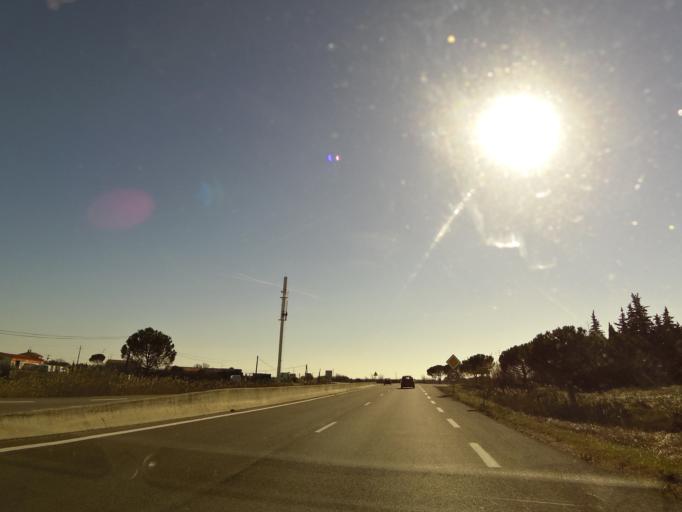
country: FR
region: Languedoc-Roussillon
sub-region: Departement de l'Herault
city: Marsillargues
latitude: 43.6274
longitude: 4.1908
